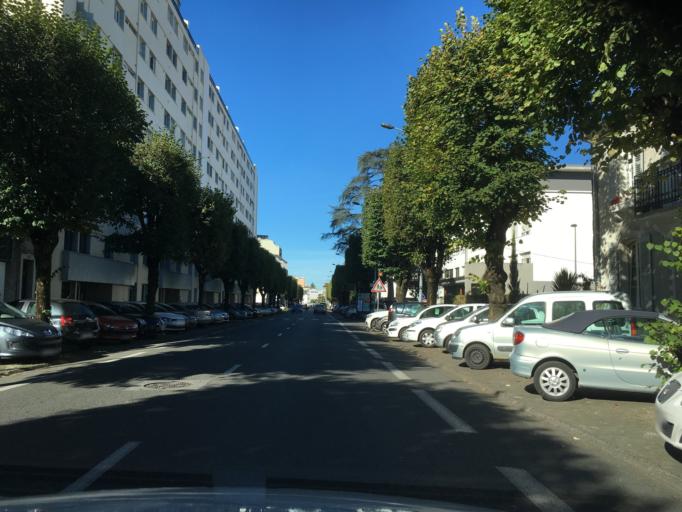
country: FR
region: Aquitaine
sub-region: Departement des Pyrenees-Atlantiques
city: Pau
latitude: 43.3033
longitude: -0.3637
